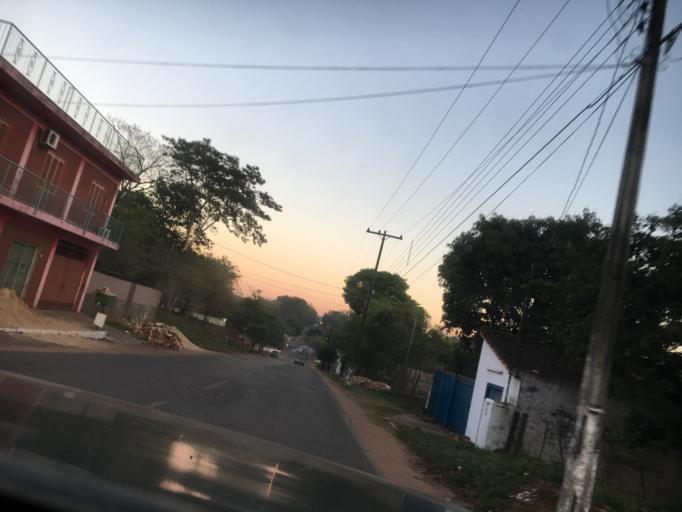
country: PY
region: Central
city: Villa Elisa
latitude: -25.3624
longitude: -57.5822
